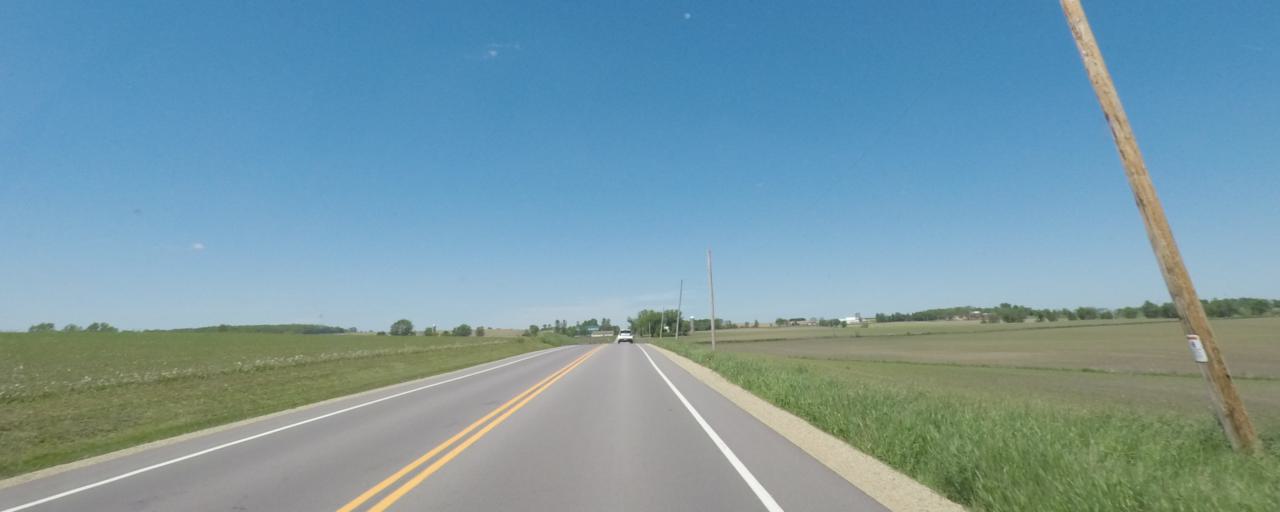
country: US
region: Wisconsin
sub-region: Green County
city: Brooklyn
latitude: 42.8091
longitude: -89.3692
